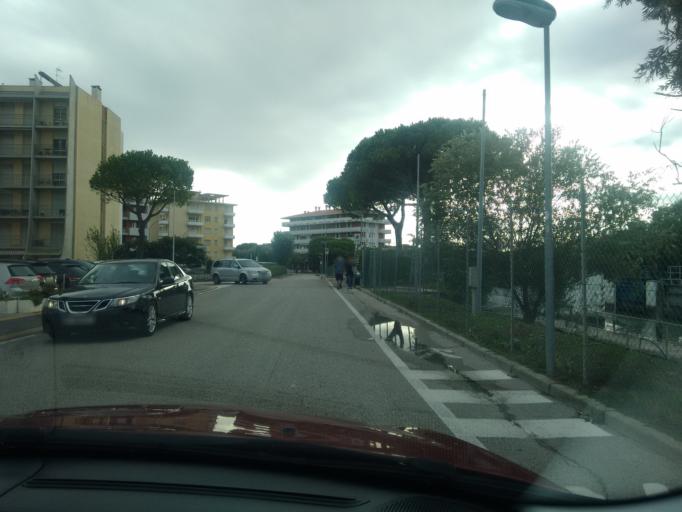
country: IT
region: Veneto
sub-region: Provincia di Venezia
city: Caorle
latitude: 45.5897
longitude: 12.8619
